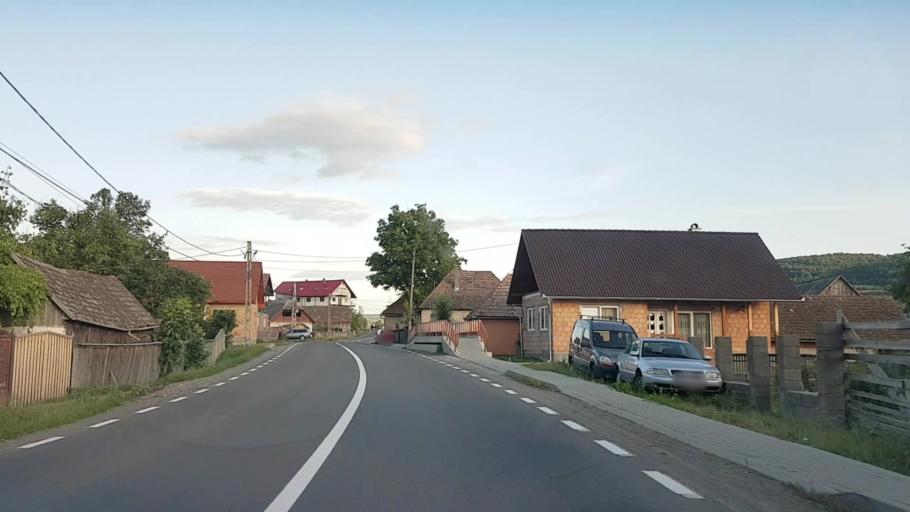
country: RO
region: Harghita
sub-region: Comuna Praid
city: Ocna de Sus
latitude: 46.5183
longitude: 25.1526
